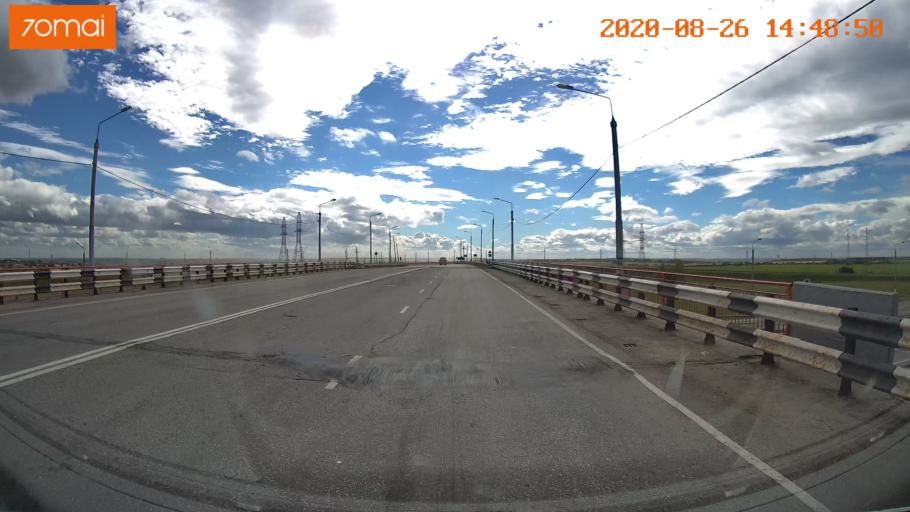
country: RU
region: Rjazan
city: Mikhaylov
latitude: 54.2632
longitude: 39.0060
